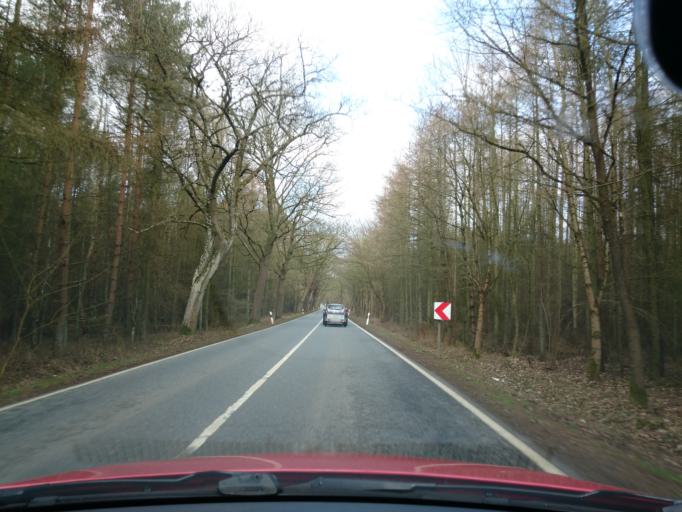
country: DE
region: Mecklenburg-Vorpommern
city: Velgast
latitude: 54.2852
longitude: 12.7983
